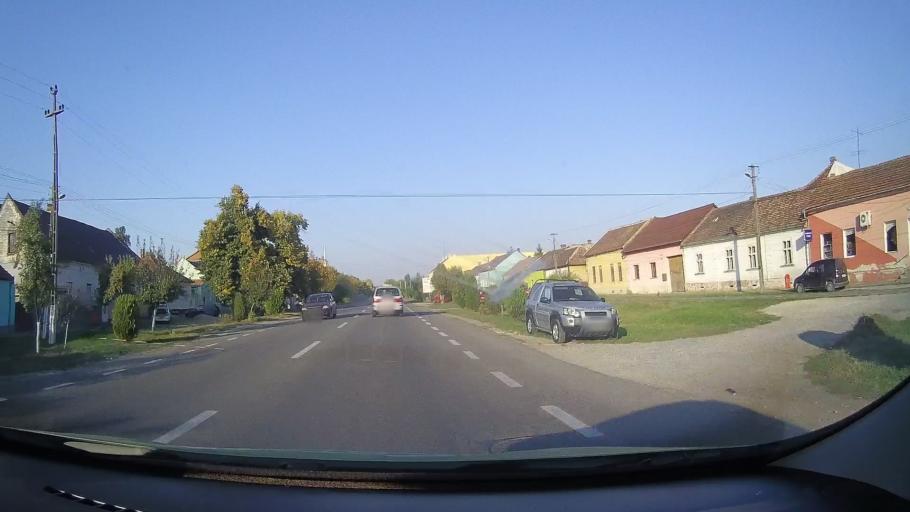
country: RO
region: Arad
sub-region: Comuna Pancota
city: Pancota
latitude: 46.3205
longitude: 21.6854
